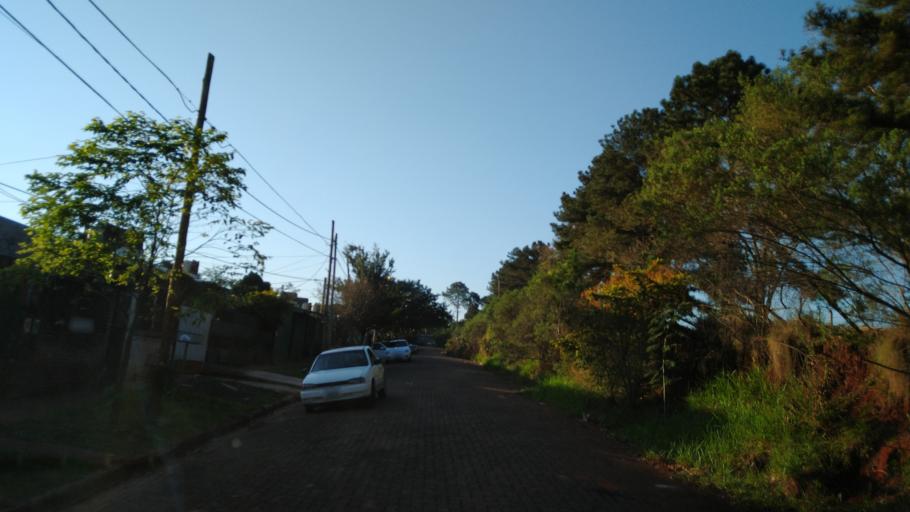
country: AR
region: Misiones
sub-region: Departamento de Capital
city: Posadas
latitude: -27.4306
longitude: -55.9231
